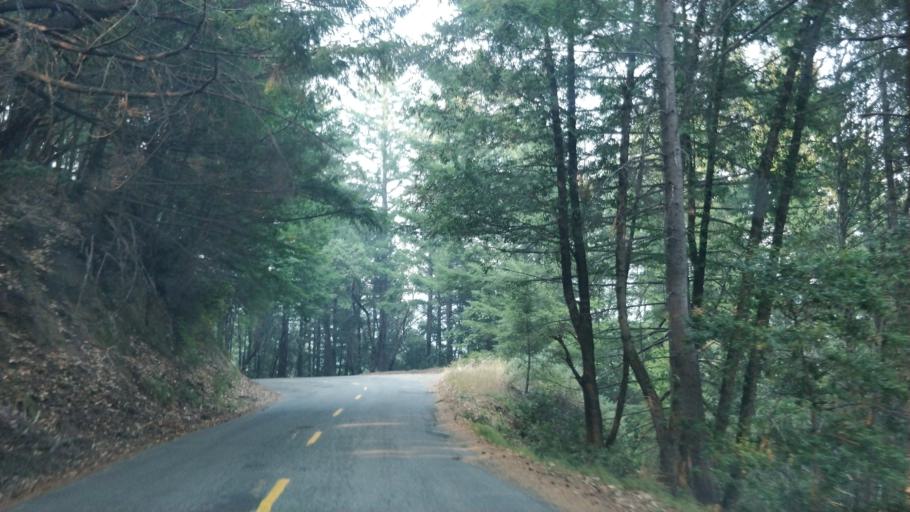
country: US
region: California
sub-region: Humboldt County
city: Rio Dell
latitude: 40.2680
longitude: -124.0767
